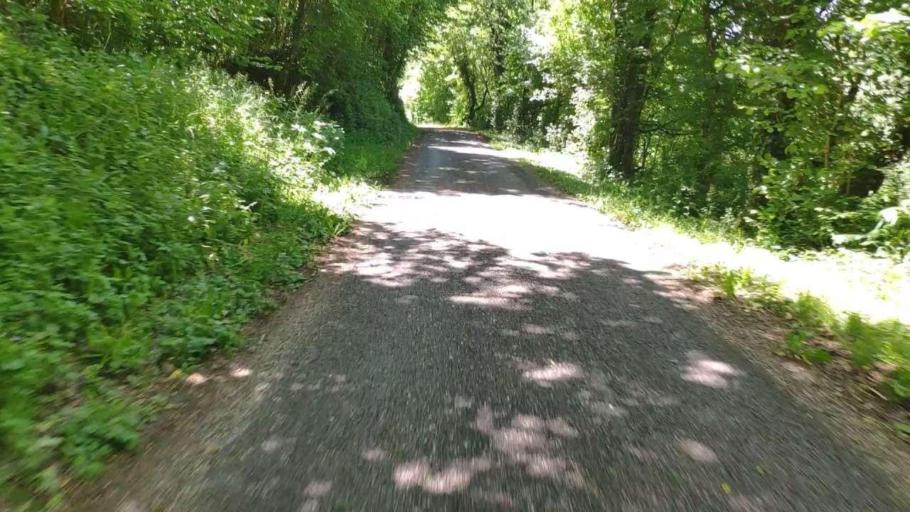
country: FR
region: Franche-Comte
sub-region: Departement du Jura
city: Poligny
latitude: 46.7546
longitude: 5.6752
